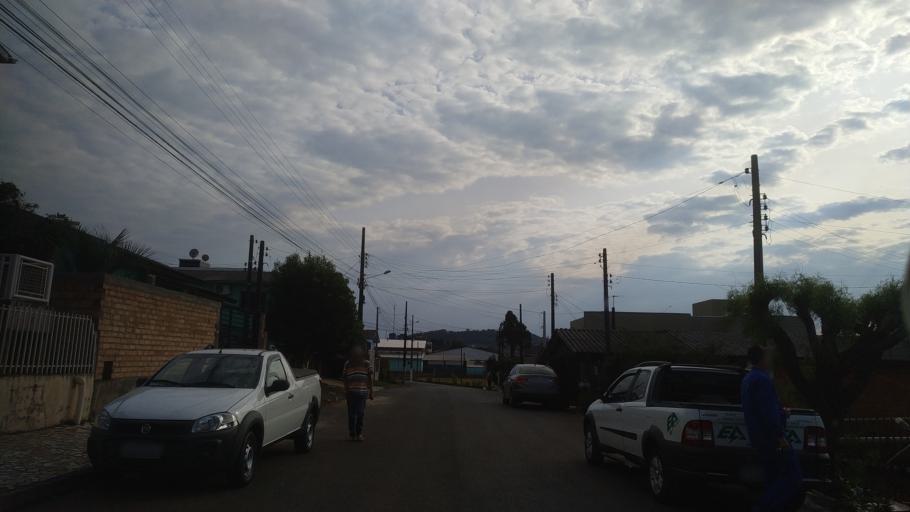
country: BR
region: Santa Catarina
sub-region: Chapeco
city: Chapeco
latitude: -27.1006
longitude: -52.6864
